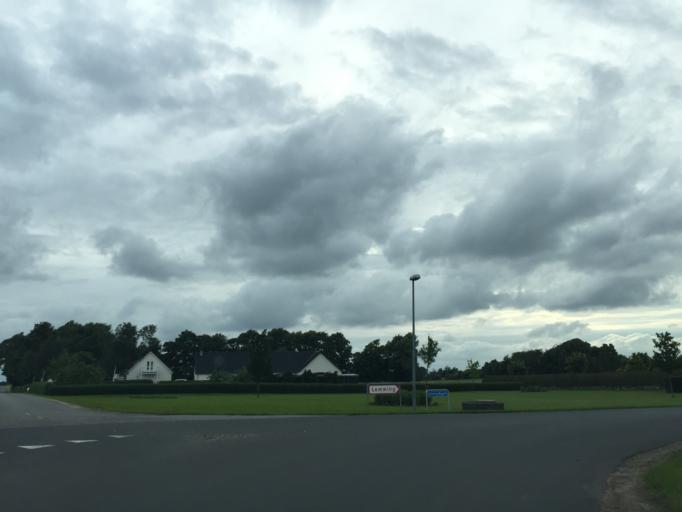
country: DK
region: Central Jutland
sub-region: Silkeborg Kommune
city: Silkeborg
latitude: 56.2353
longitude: 9.5471
